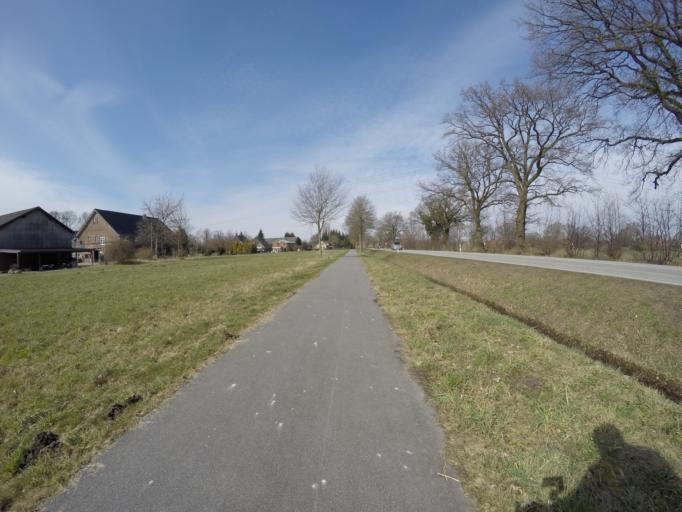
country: DE
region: Schleswig-Holstein
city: Bilsen
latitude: 53.7647
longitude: 9.8782
